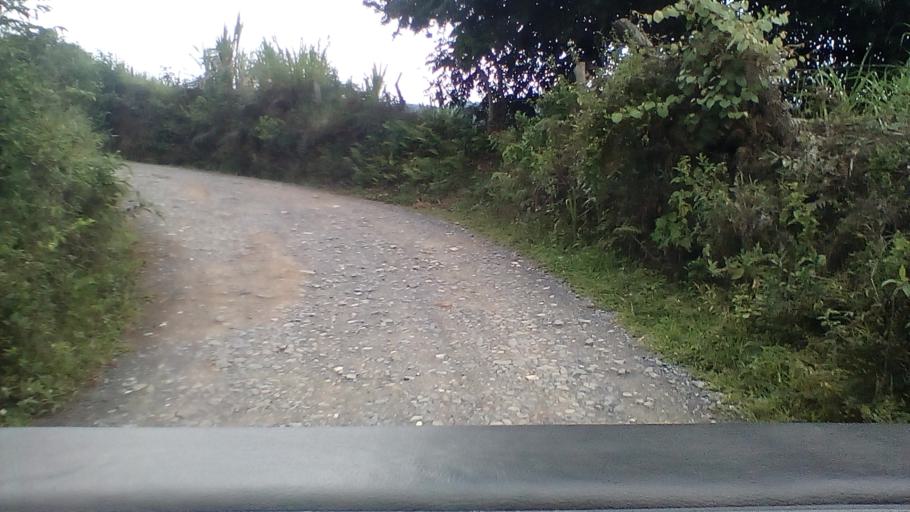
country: CO
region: Boyaca
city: Santana
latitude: 6.0221
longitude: -73.5155
